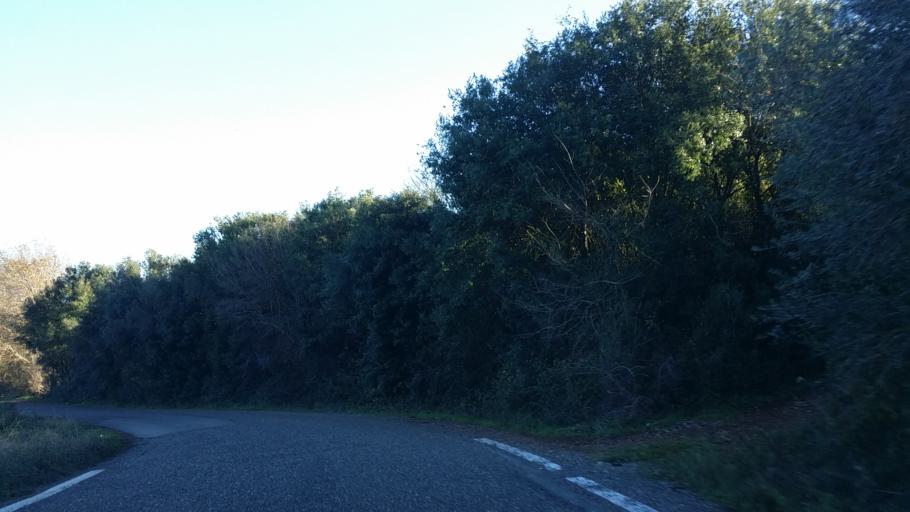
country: GR
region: West Greece
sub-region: Nomos Aitolias kai Akarnanias
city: Fitiai
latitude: 38.6228
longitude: 21.2116
